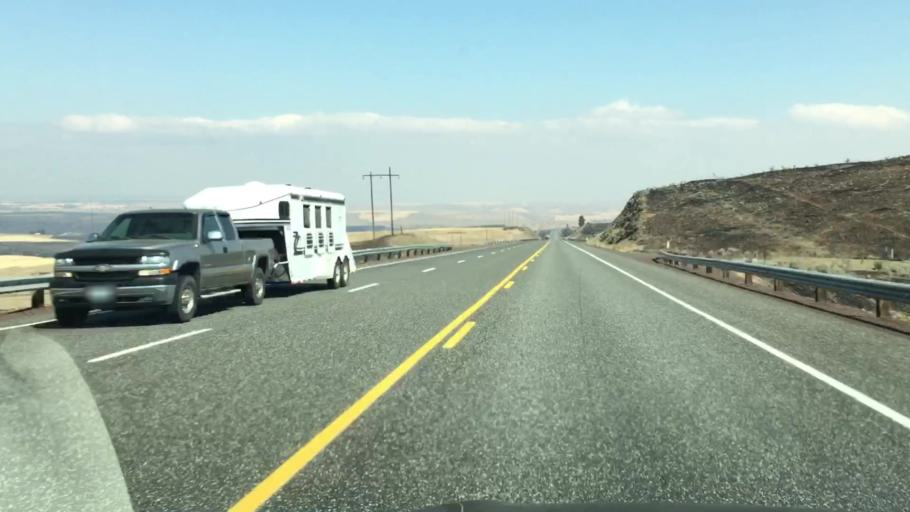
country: US
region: Oregon
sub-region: Wasco County
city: The Dalles
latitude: 45.3688
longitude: -121.1417
